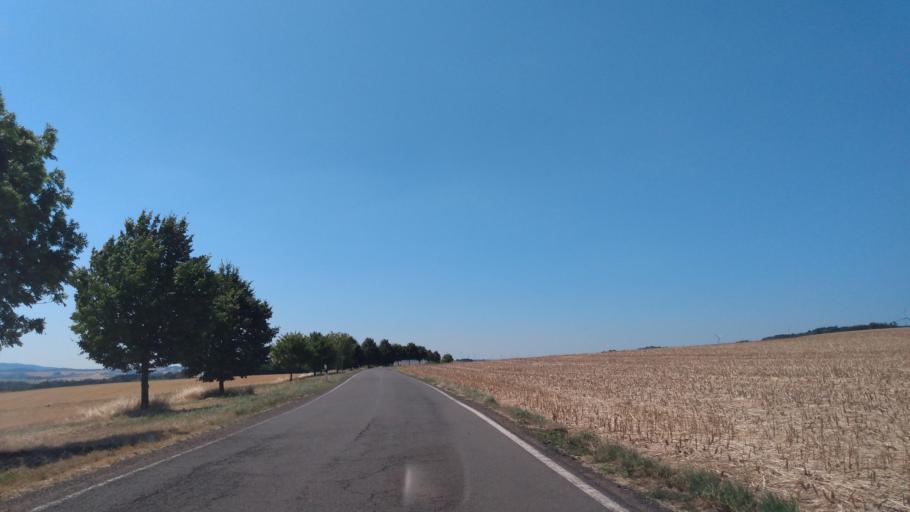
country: DE
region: Rheinland-Pfalz
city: Morbach
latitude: 49.8265
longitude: 7.0787
